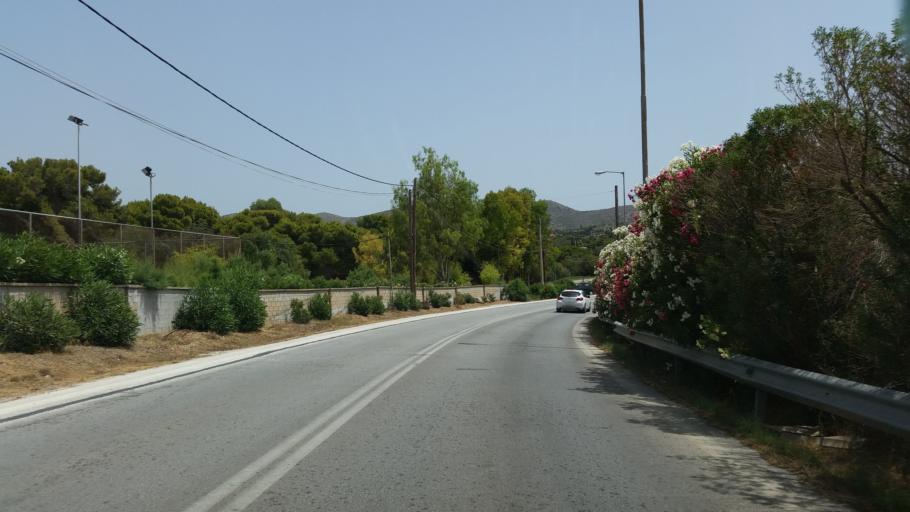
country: GR
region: Attica
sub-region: Nomarchia Anatolikis Attikis
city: Palaia Fokaia
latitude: 37.7047
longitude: 23.9394
